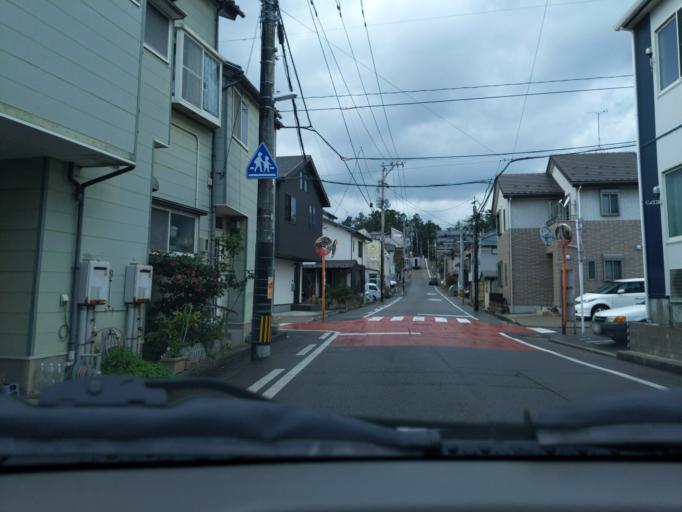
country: JP
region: Niigata
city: Niigata-shi
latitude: 37.9299
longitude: 139.0427
